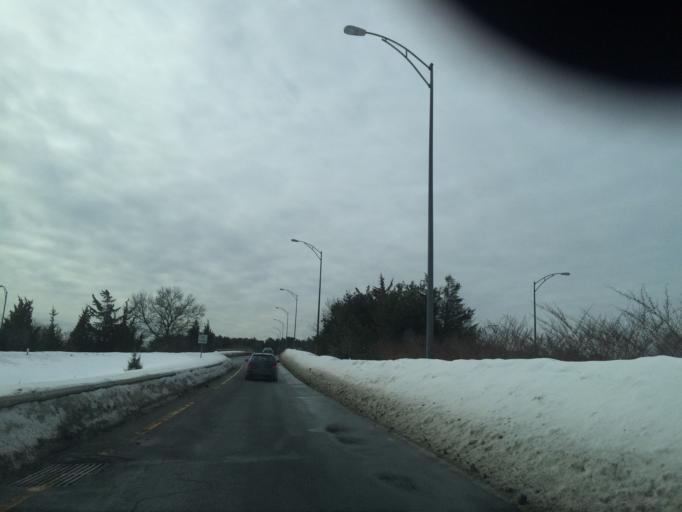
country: US
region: Massachusetts
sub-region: Middlesex County
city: Weston
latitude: 42.3421
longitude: -71.2653
